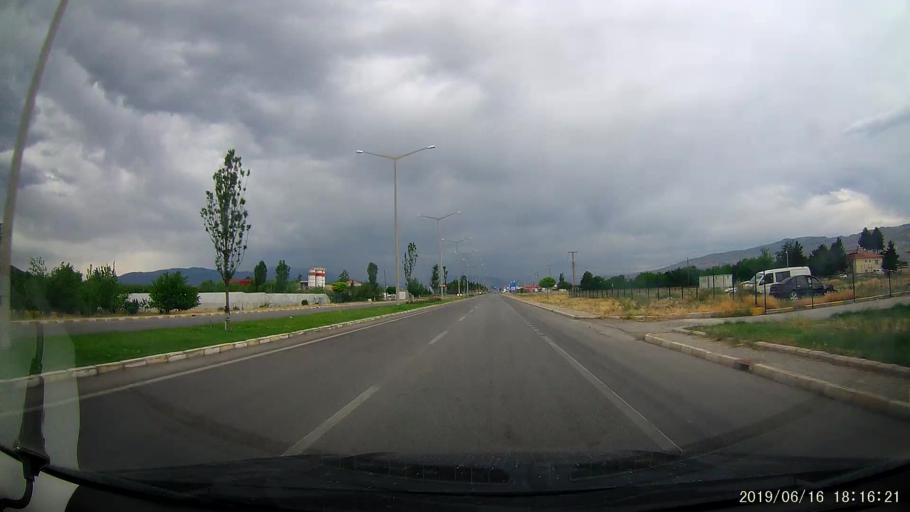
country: TR
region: Erzincan
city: Erzincan
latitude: 39.7279
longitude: 39.5490
